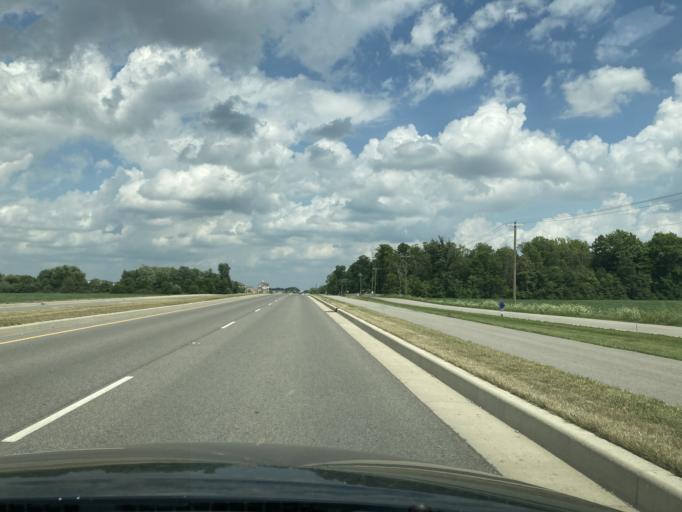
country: US
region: Indiana
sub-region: Hamilton County
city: Carmel
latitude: 39.9994
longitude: -86.1958
